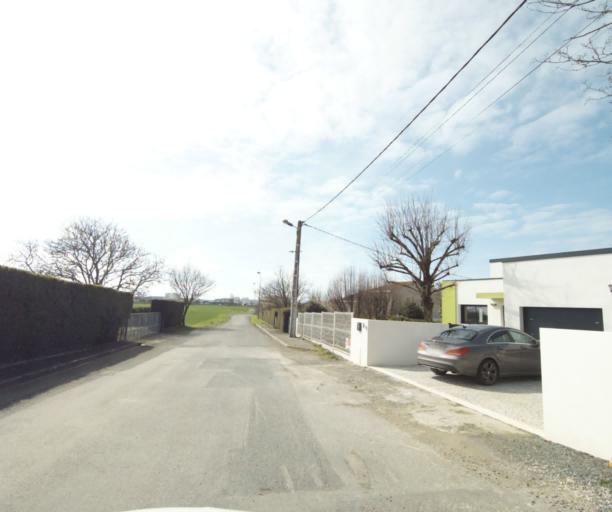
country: FR
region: Poitou-Charentes
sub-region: Departement de la Charente-Maritime
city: Lagord
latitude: 46.1796
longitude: -1.1647
